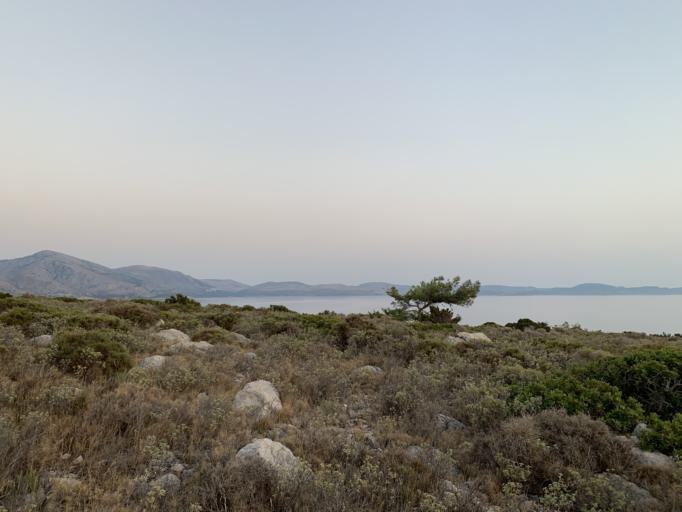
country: GR
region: North Aegean
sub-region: Chios
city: Vrontados
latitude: 38.4045
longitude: 25.9615
